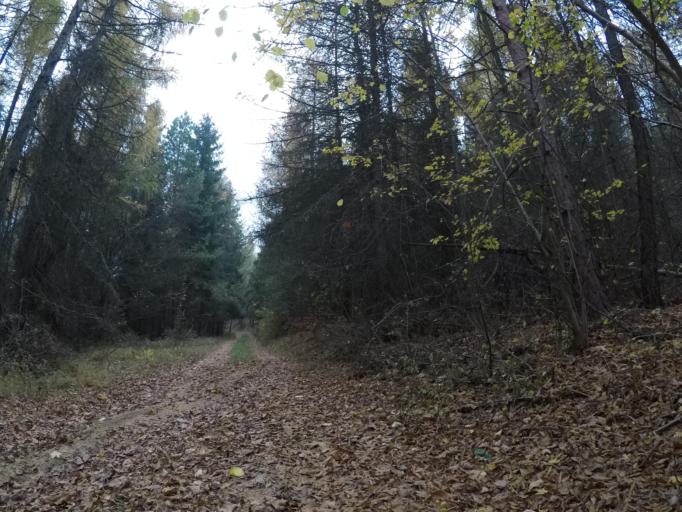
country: SK
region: Presovsky
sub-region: Okres Presov
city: Presov
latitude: 48.9010
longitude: 21.1676
